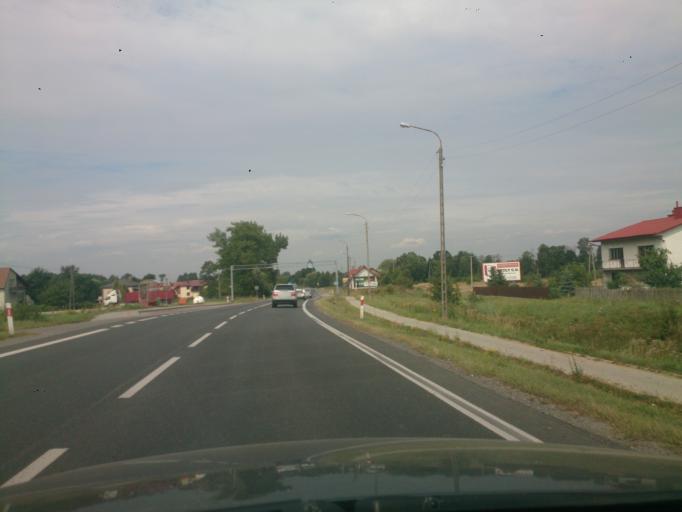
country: PL
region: Subcarpathian Voivodeship
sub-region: Powiat kolbuszowski
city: Kolbuszowa
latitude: 50.2143
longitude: 21.8152
